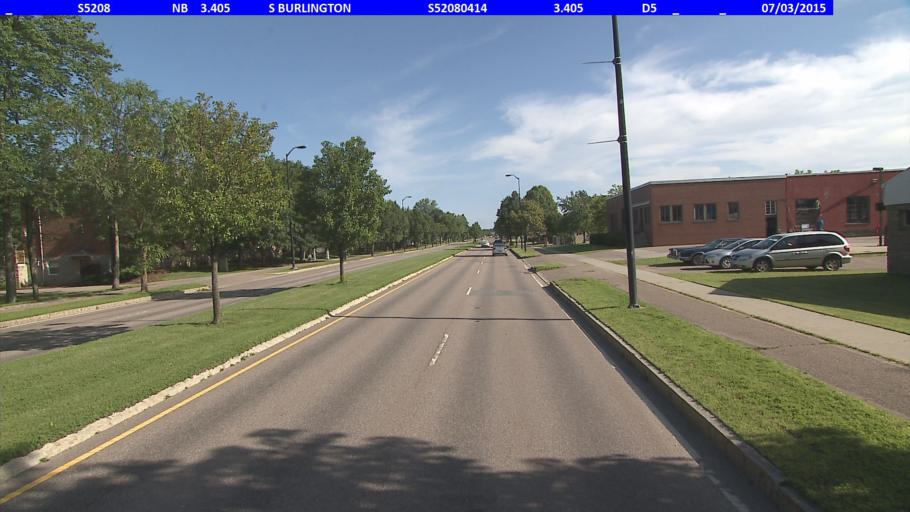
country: US
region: Vermont
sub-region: Chittenden County
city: South Burlington
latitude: 44.4592
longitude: -73.1797
